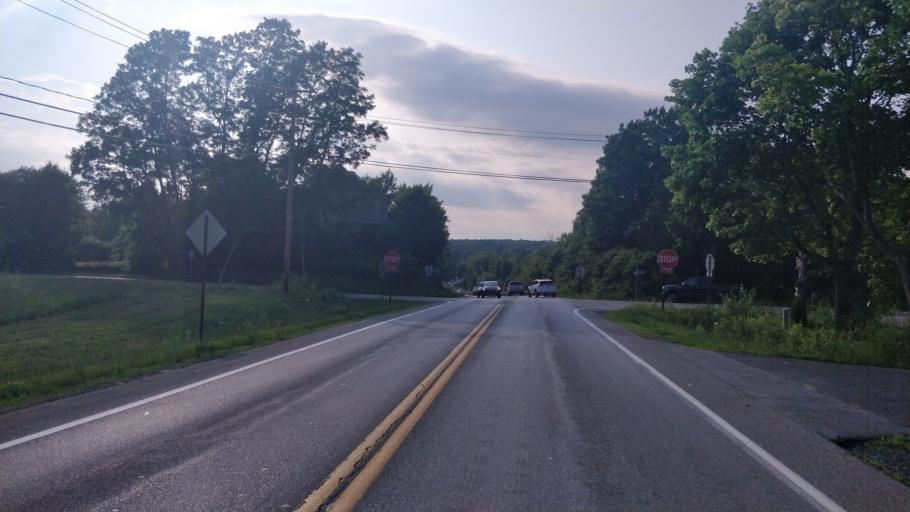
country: US
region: New York
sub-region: Saratoga County
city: North Ballston Spa
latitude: 43.0181
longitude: -73.8237
